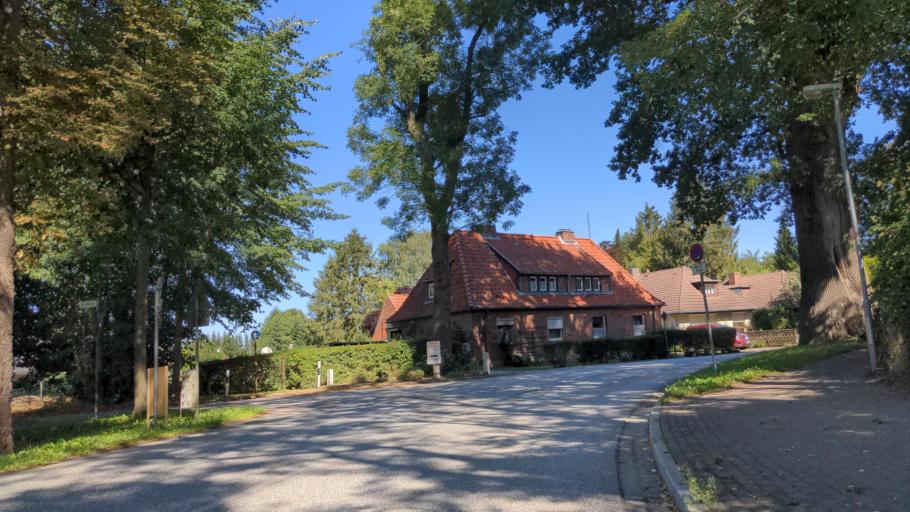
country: DE
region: Schleswig-Holstein
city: Hamberge
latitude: 53.8327
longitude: 10.6098
